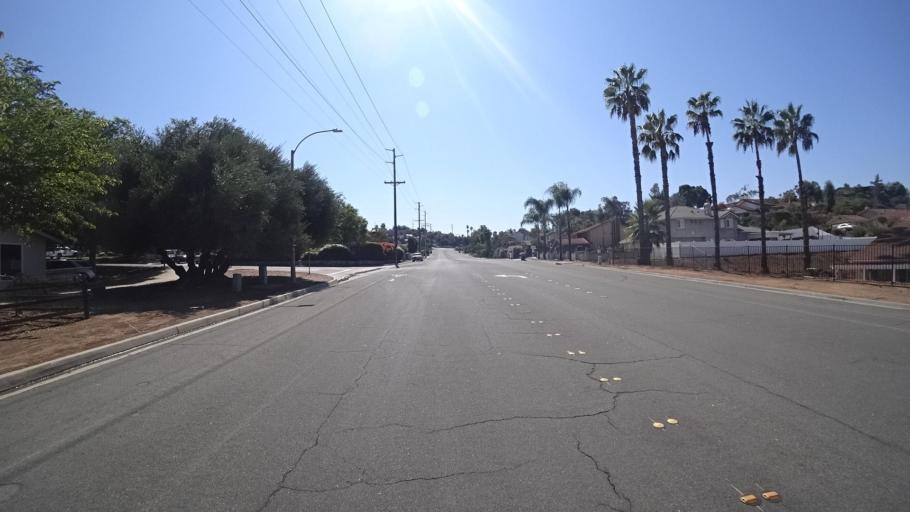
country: US
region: California
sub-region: San Diego County
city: Granite Hills
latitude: 32.7966
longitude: -116.9024
